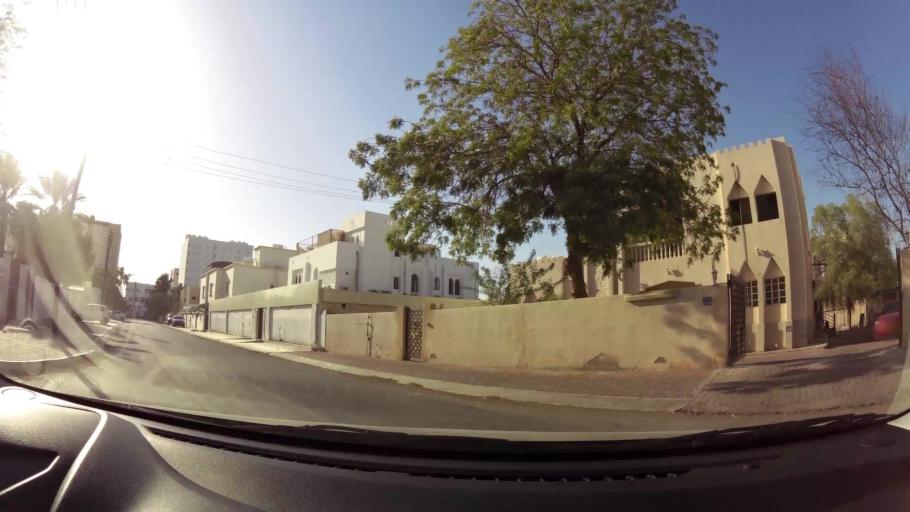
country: OM
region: Muhafazat Masqat
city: As Sib al Jadidah
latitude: 23.6375
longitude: 58.2046
